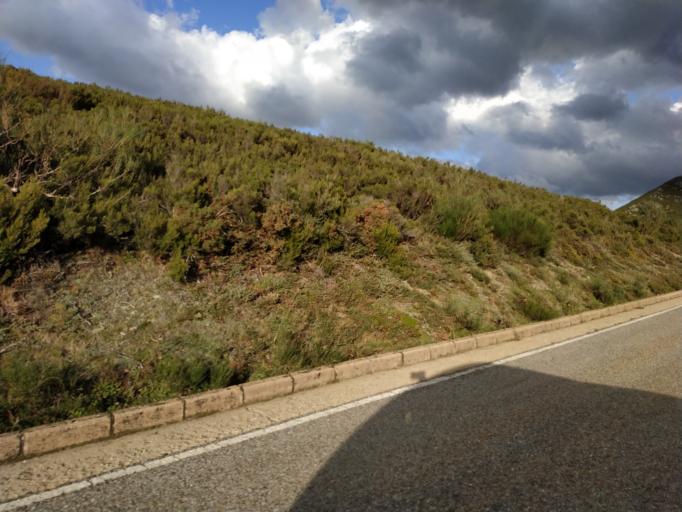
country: ES
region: Castille and Leon
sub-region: Provincia de Leon
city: Candin
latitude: 42.8738
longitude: -6.8248
